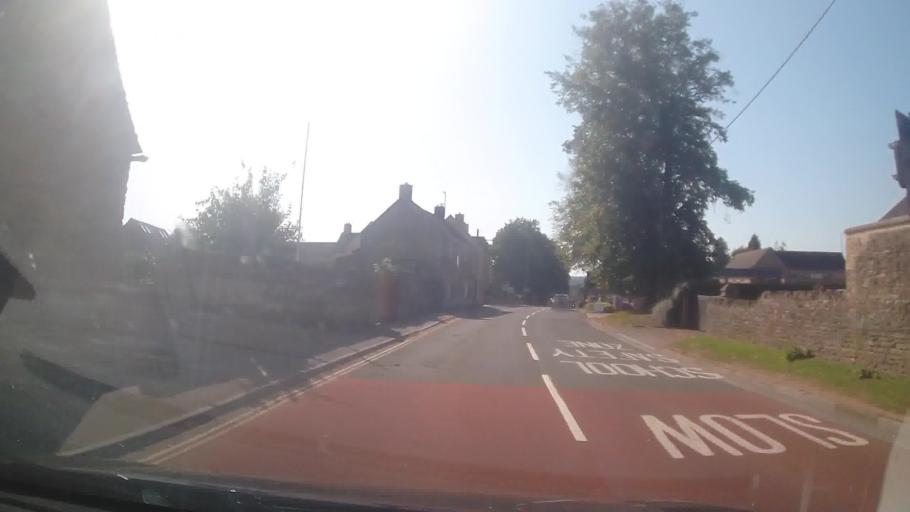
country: GB
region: England
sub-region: Gloucestershire
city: Bourton on the Water
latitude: 51.8860
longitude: -1.7541
